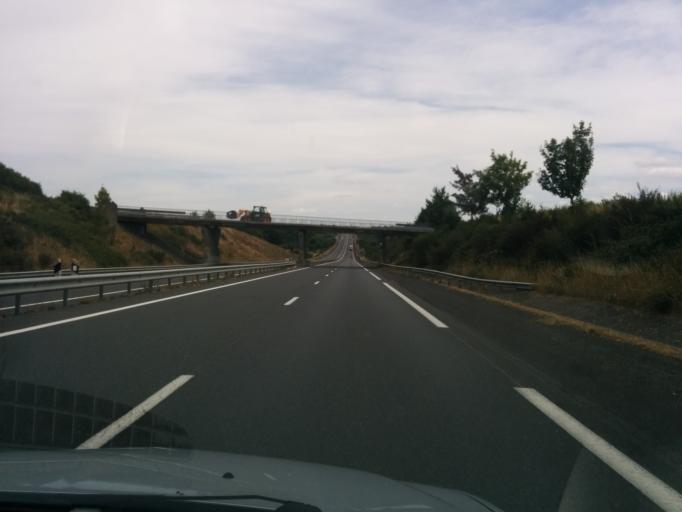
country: FR
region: Poitou-Charentes
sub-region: Departement des Deux-Sevres
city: Bressuire
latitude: 46.8581
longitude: -0.4978
